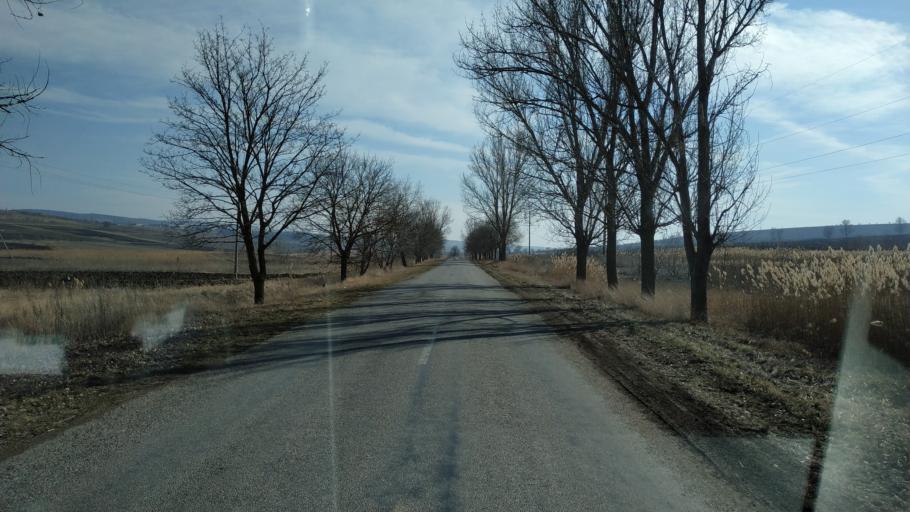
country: MD
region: Nisporeni
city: Nisporeni
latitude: 47.0974
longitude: 28.1316
